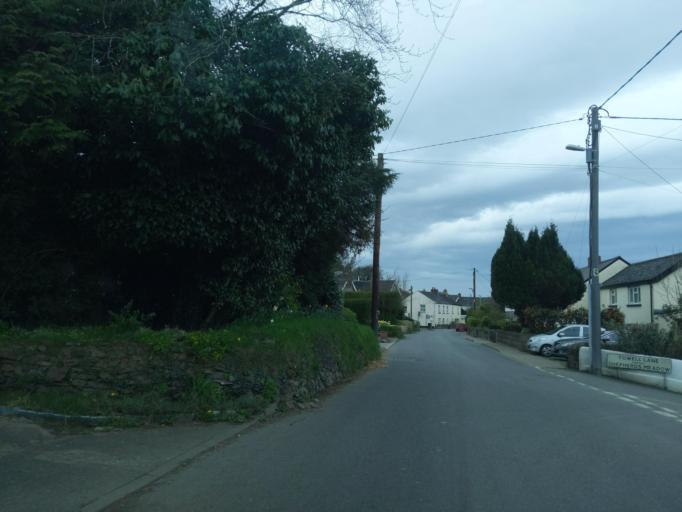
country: GB
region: England
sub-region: Devon
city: Great Torrington
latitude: 50.9156
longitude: -4.0579
